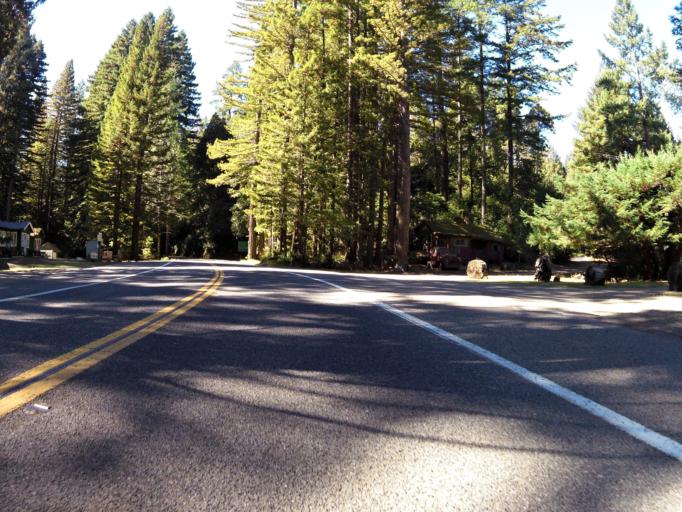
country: US
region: California
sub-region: Humboldt County
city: Redway
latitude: 39.8178
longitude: -123.7822
